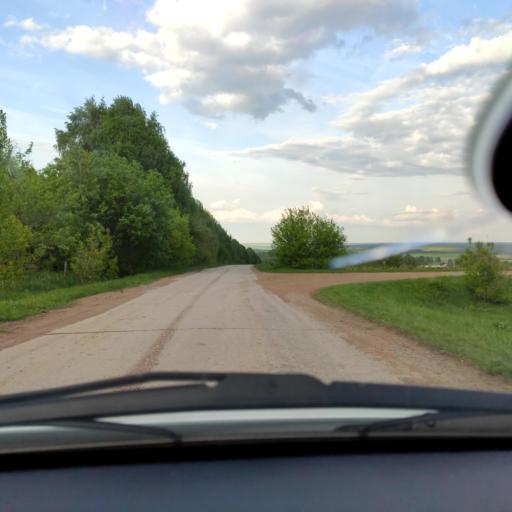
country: RU
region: Bashkortostan
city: Dyurtyuli
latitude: 55.5919
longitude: 54.9427
